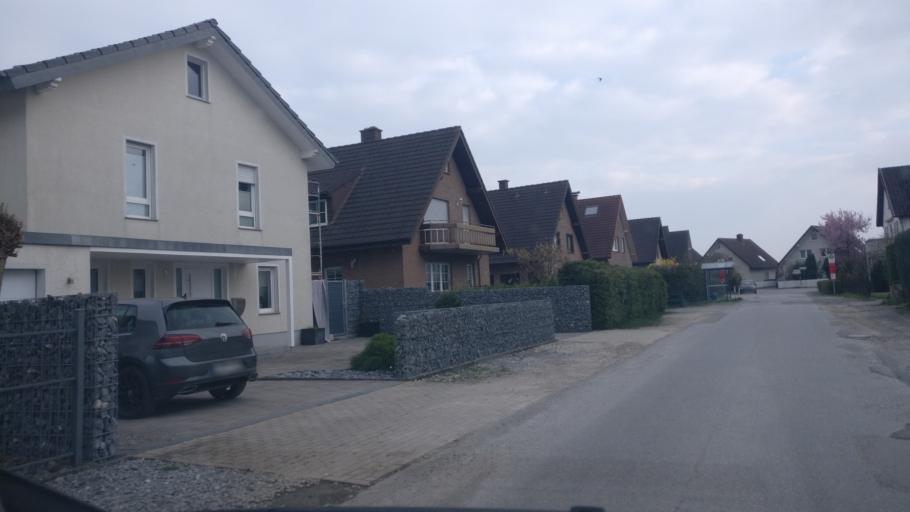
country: DE
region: North Rhine-Westphalia
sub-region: Regierungsbezirk Detmold
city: Lage
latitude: 52.0210
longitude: 8.7657
